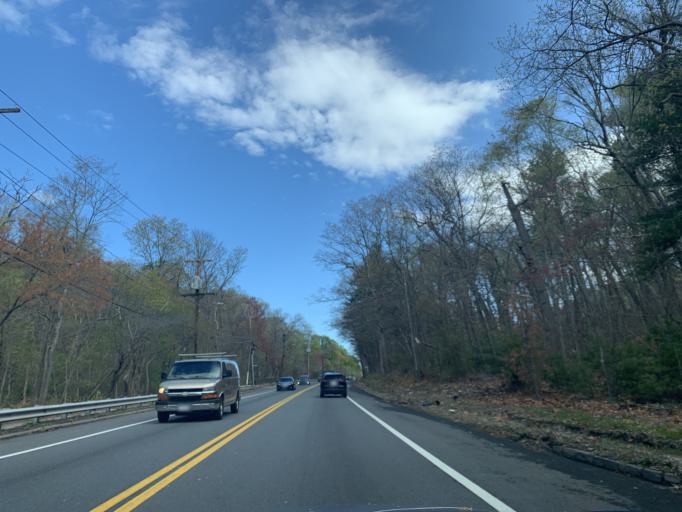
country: US
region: Massachusetts
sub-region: Norfolk County
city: Dedham
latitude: 42.2138
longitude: -71.1199
